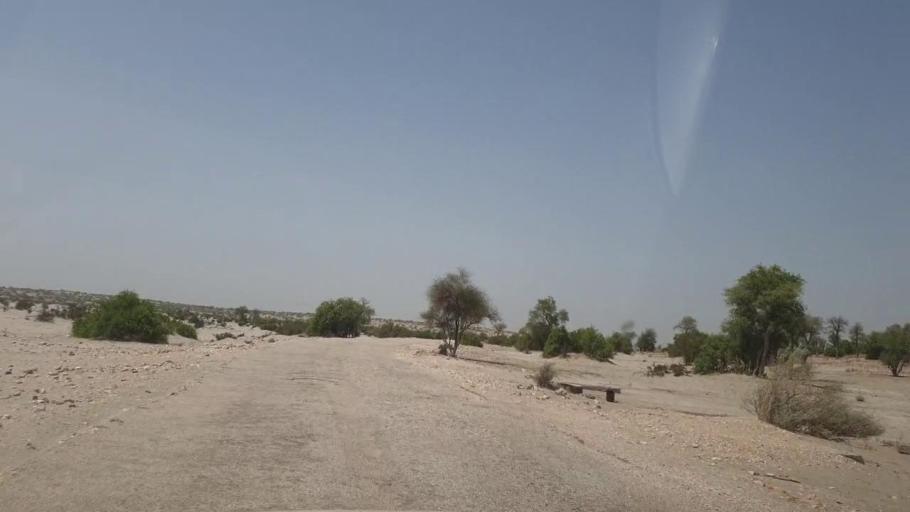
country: PK
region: Sindh
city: Khanpur
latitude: 27.3395
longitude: 69.3149
